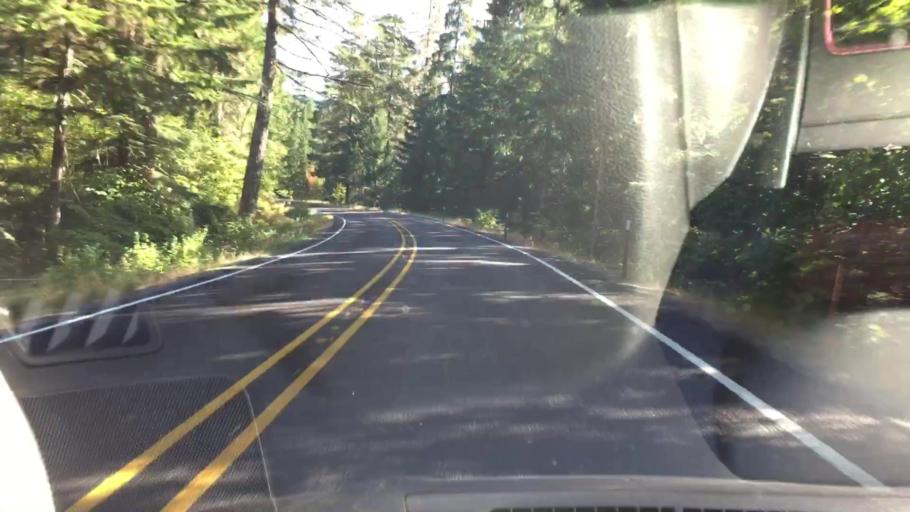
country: US
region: Washington
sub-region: Pierce County
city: Buckley
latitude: 46.7004
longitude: -121.5825
